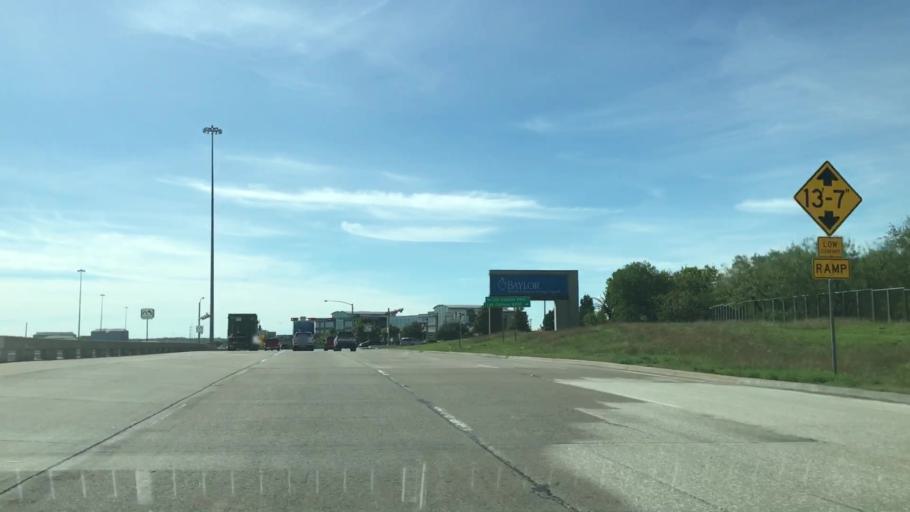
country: US
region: Texas
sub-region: Dallas County
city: Farmers Branch
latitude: 32.9093
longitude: -96.9519
